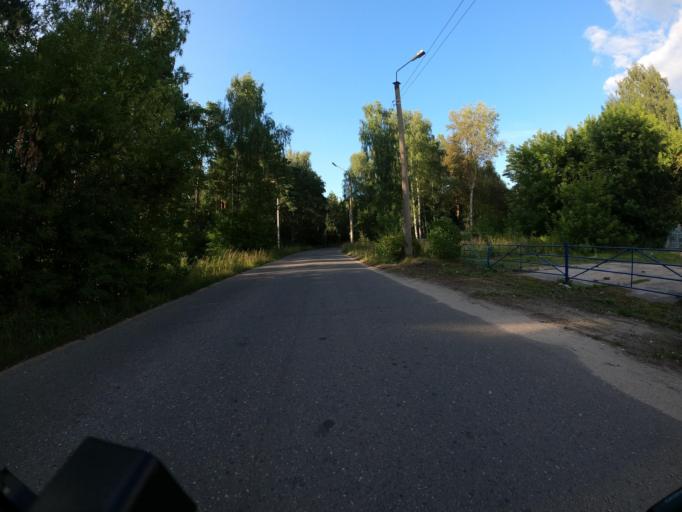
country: RU
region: Moskovskaya
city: Beloozerskiy
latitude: 55.4555
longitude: 38.4910
